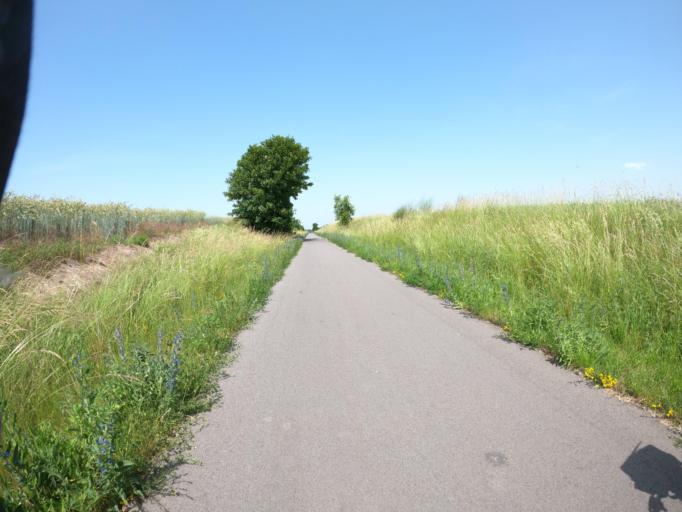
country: PL
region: West Pomeranian Voivodeship
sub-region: Powiat choszczenski
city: Choszczno
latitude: 53.1483
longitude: 15.3724
